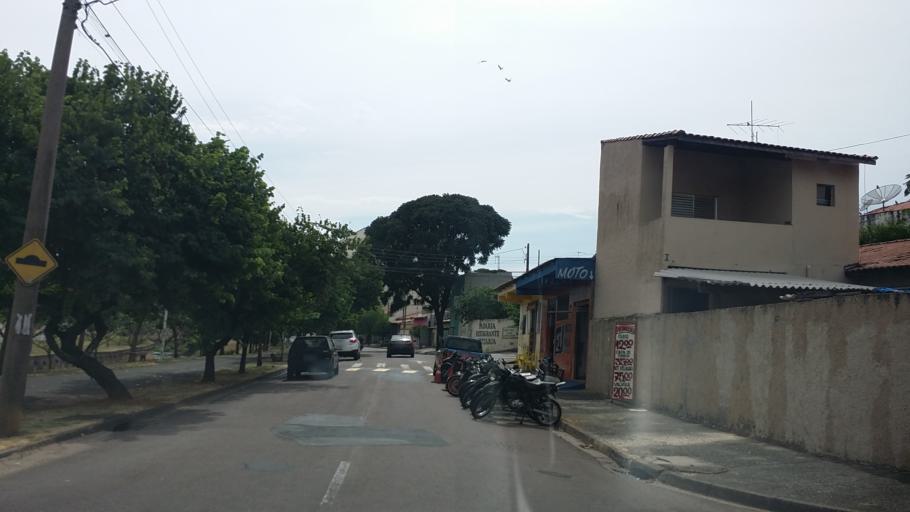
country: BR
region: Sao Paulo
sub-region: Indaiatuba
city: Indaiatuba
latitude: -23.0966
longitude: -47.2213
